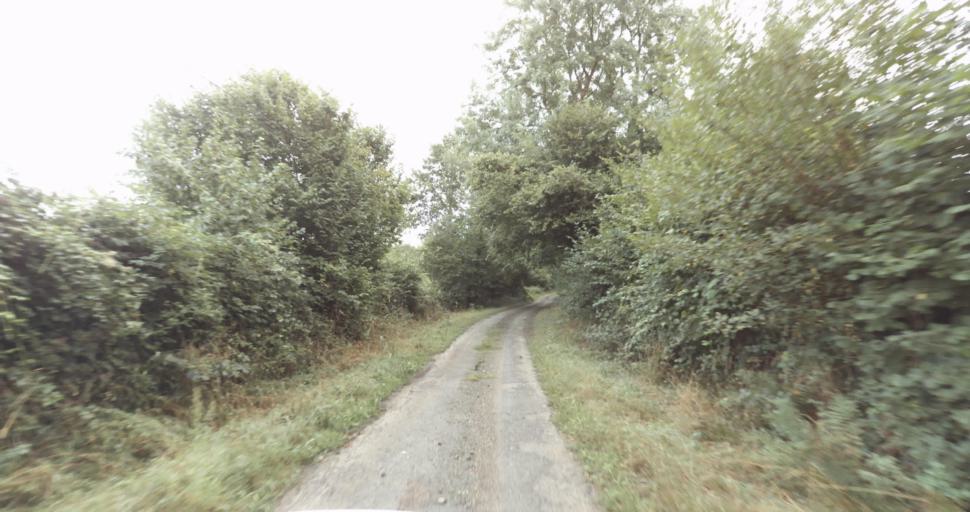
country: FR
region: Lower Normandy
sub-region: Departement de l'Orne
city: Trun
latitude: 48.9047
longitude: 0.1023
